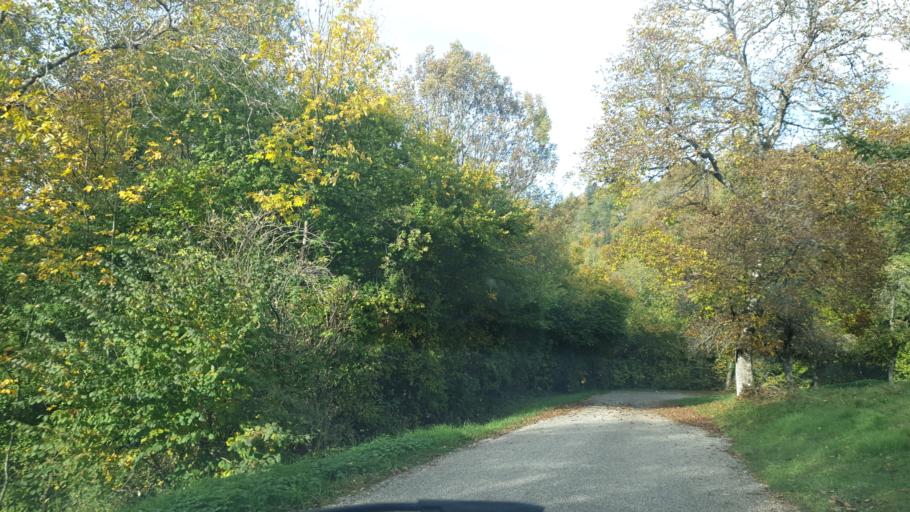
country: FR
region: Rhone-Alpes
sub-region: Departement de la Savoie
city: Coise-Saint-Jean-Pied-Gauthier
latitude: 45.4776
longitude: 6.1835
